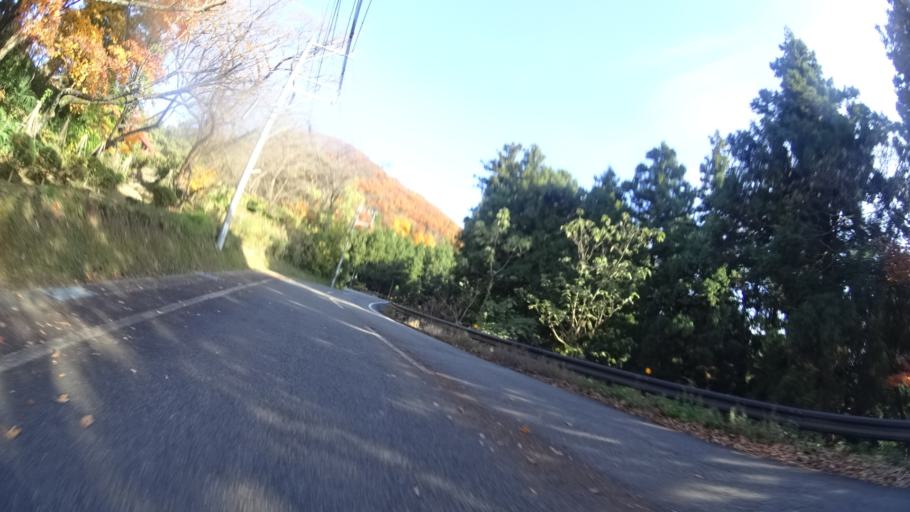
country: JP
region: Niigata
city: Yoshida-kasugacho
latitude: 37.6636
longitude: 138.8148
